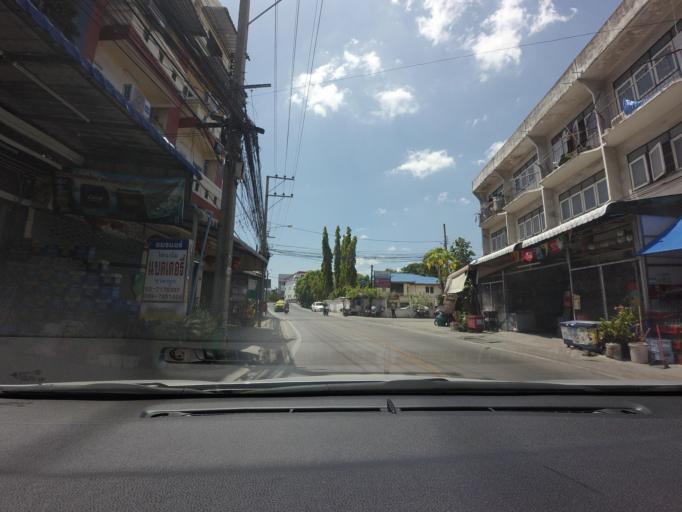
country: TH
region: Bangkok
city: Watthana
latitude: 13.7275
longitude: 100.6114
